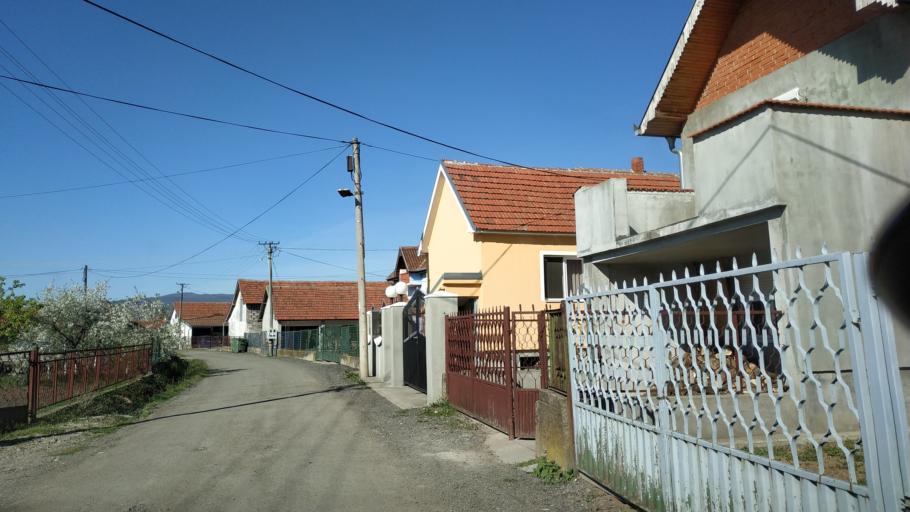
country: RS
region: Central Serbia
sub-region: Nisavski Okrug
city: Aleksinac
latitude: 43.5104
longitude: 21.6870
